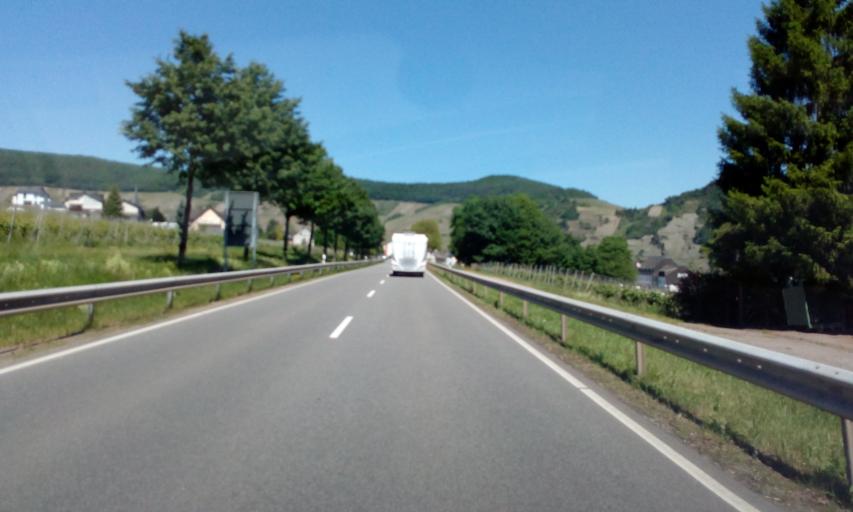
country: DE
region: Rheinland-Pfalz
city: Minheim
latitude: 49.8715
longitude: 6.9255
